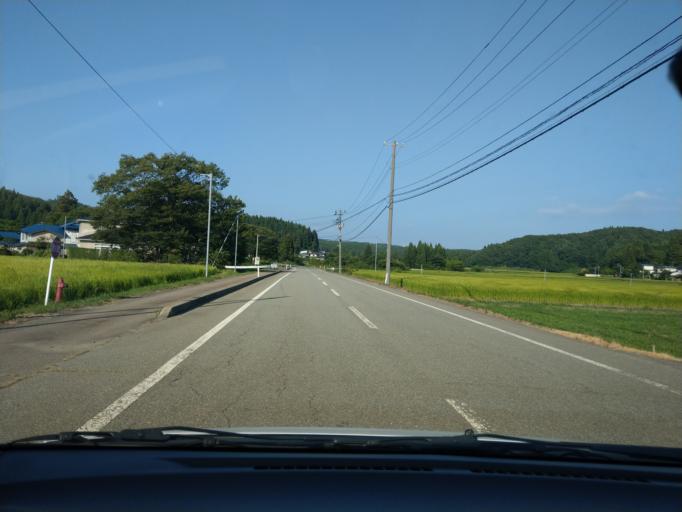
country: JP
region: Akita
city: Akita
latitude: 39.5993
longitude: 140.2137
